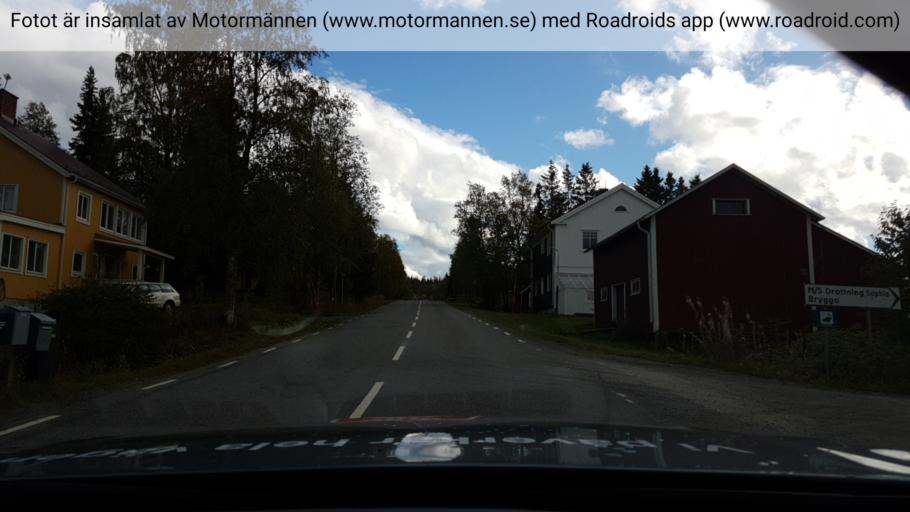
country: SE
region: Jaemtland
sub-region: Are Kommun
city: Are
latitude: 63.5602
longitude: 13.0260
